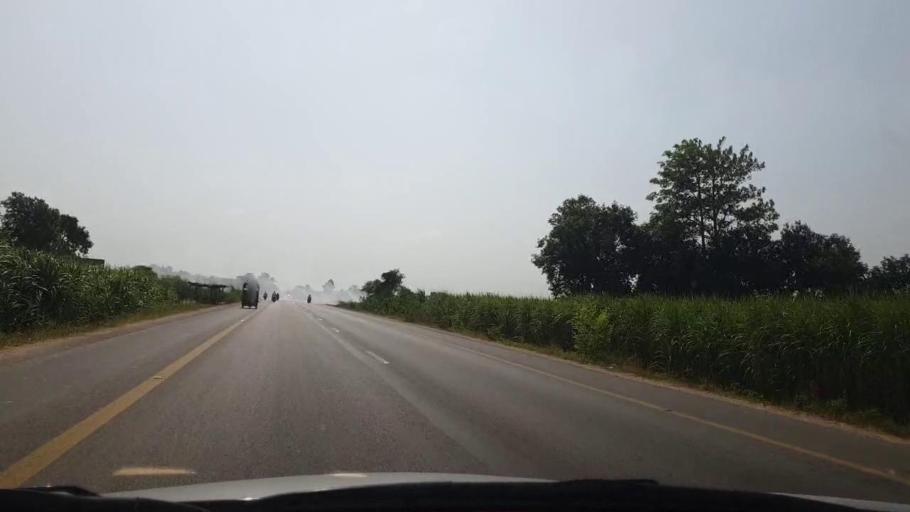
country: PK
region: Sindh
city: Matli
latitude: 25.0768
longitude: 68.6155
